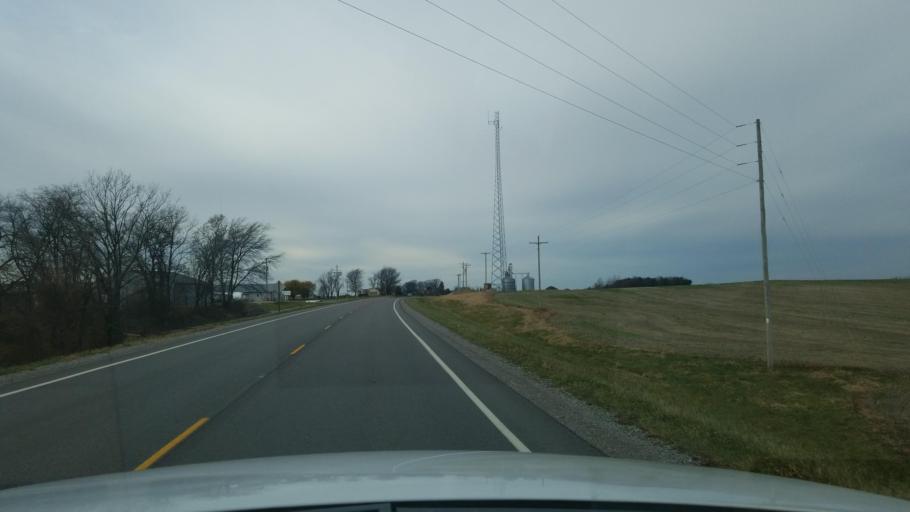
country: US
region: Illinois
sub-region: White County
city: Carmi
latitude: 37.9081
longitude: -88.1412
